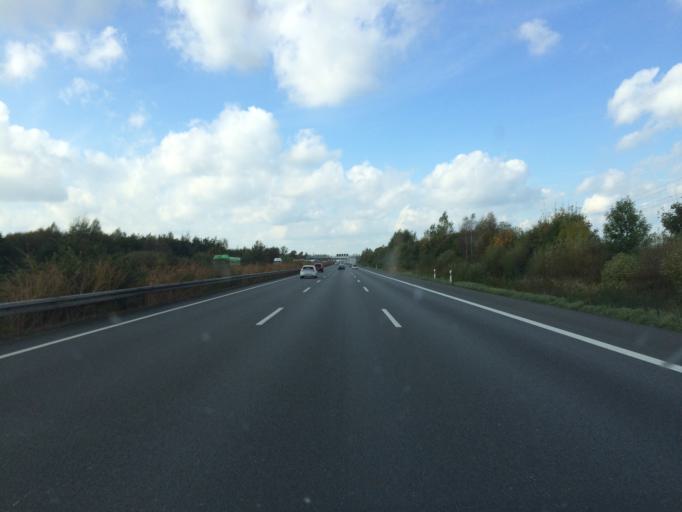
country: DE
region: Lower Saxony
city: Arpke
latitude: 52.3720
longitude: 10.0580
